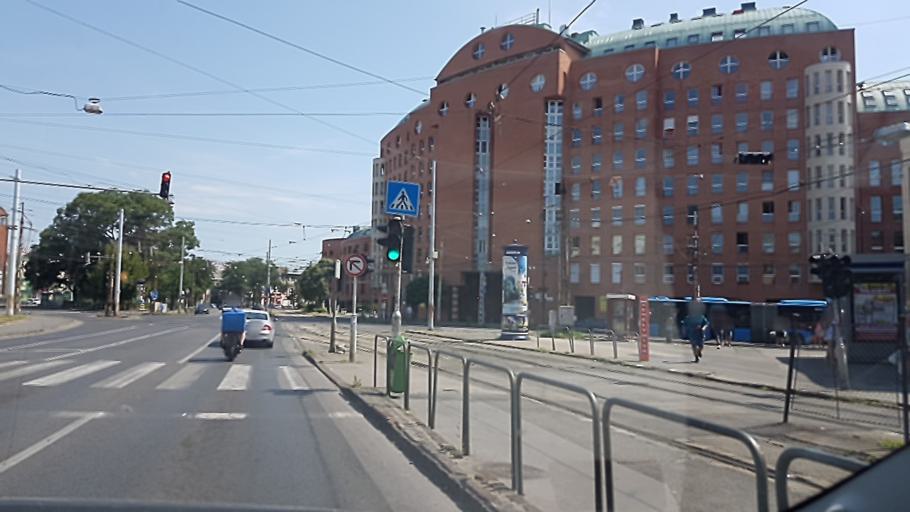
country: HU
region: Budapest
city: Budapest VIII. keruelet
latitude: 47.4899
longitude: 19.0907
